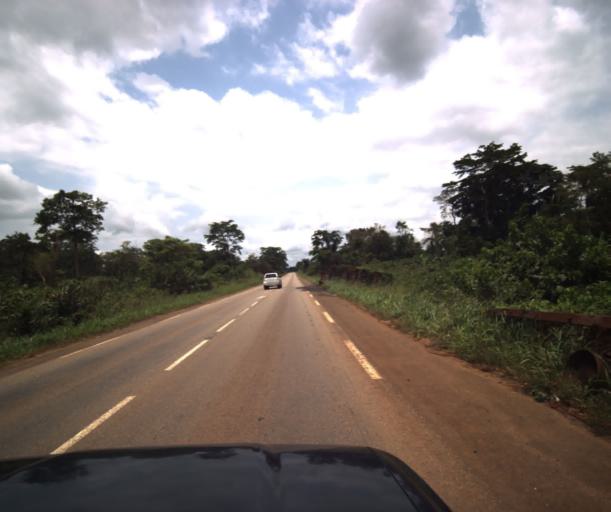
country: CM
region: Centre
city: Eseka
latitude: 3.8547
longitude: 10.9402
